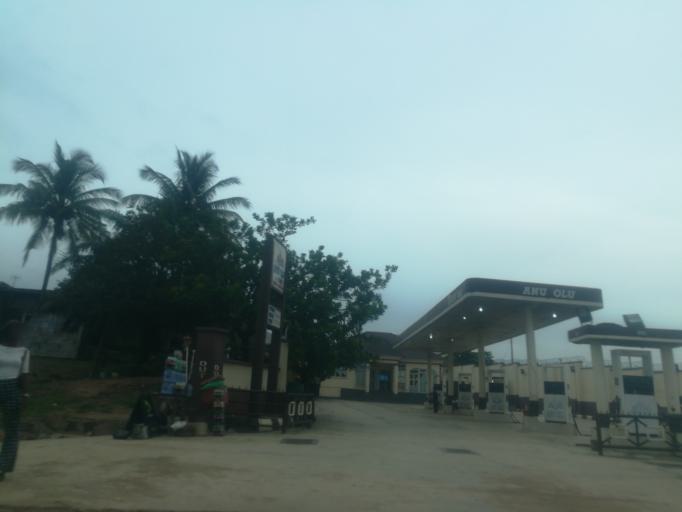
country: NG
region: Oyo
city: Egbeda
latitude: 7.3813
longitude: 3.9962
